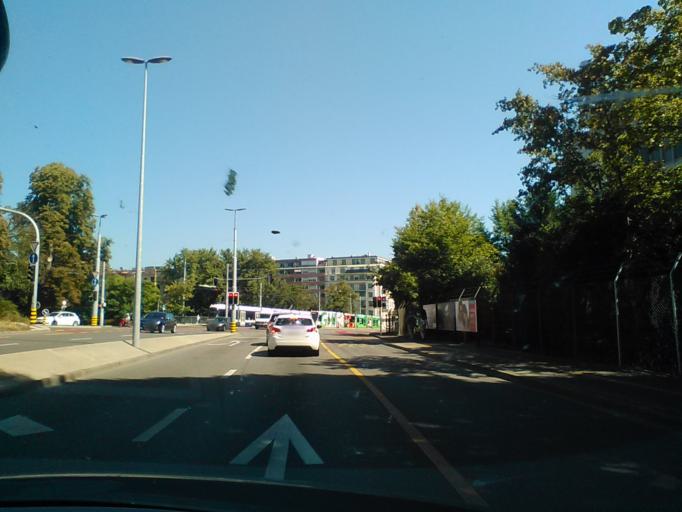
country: CH
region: Geneva
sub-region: Geneva
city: Lancy
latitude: 46.1984
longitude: 6.1280
